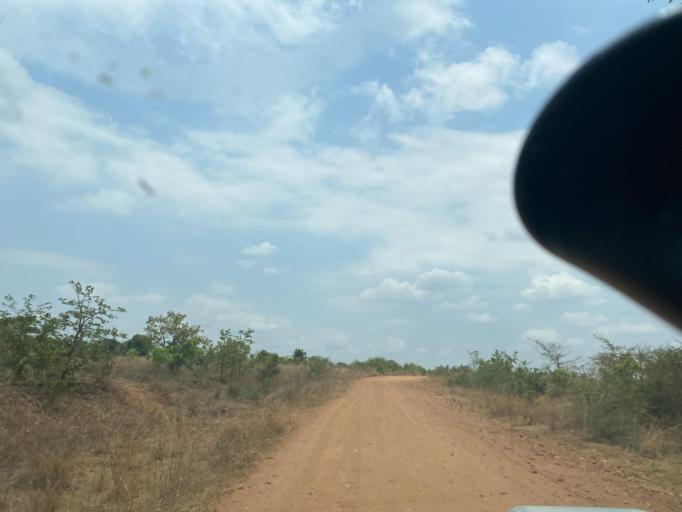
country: ZM
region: Lusaka
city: Chongwe
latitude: -15.5366
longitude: 28.8265
